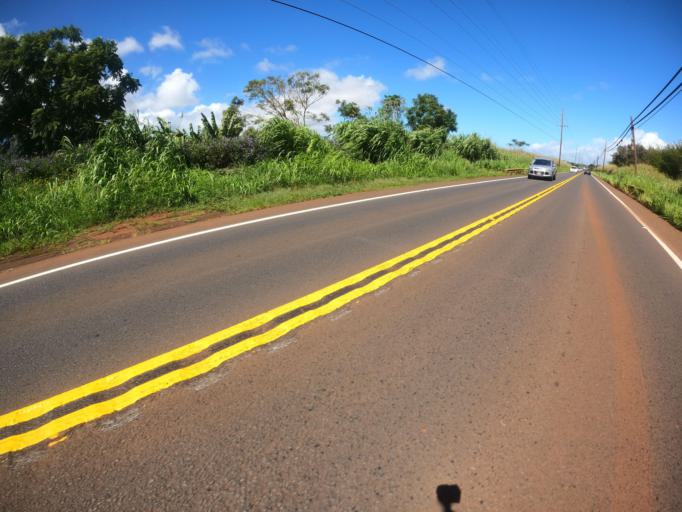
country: US
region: Hawaii
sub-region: Honolulu County
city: Schofield Barracks
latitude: 21.4633
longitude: -158.0559
